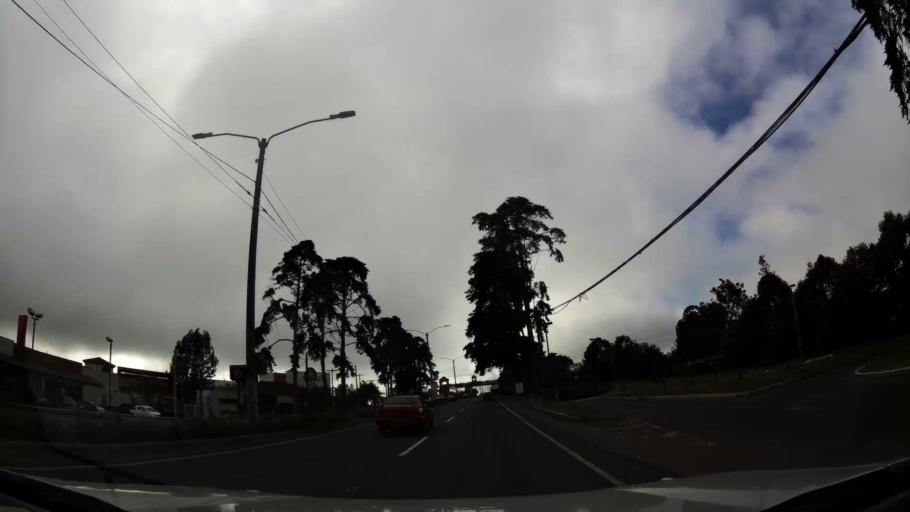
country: GT
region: Guatemala
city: Santa Catarina Pinula
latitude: 14.5533
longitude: -90.4553
